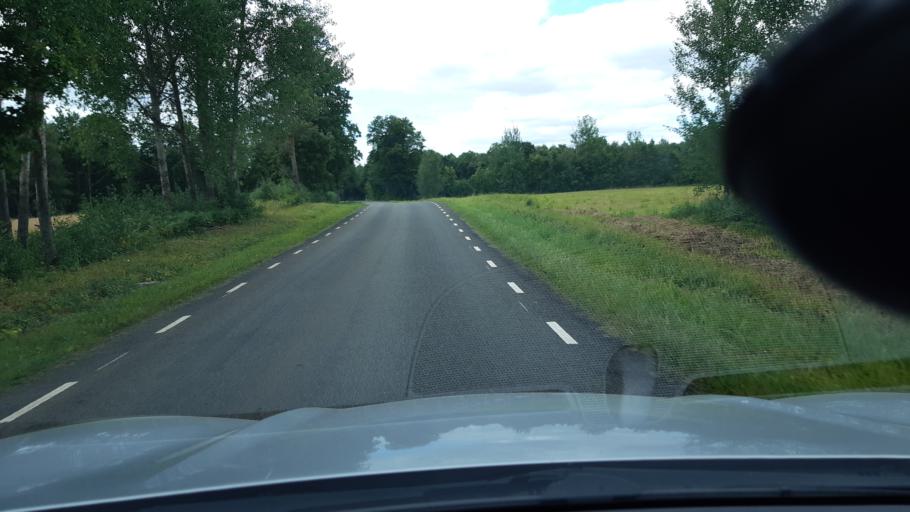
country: EE
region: Raplamaa
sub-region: Rapla vald
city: Rapla
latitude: 58.8887
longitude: 24.7198
